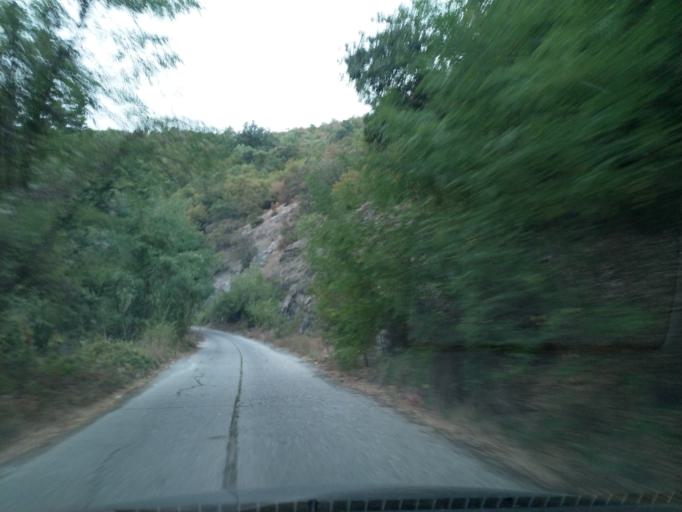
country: RS
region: Central Serbia
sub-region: Pomoravski Okrug
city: Paracin
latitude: 43.8672
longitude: 21.4593
